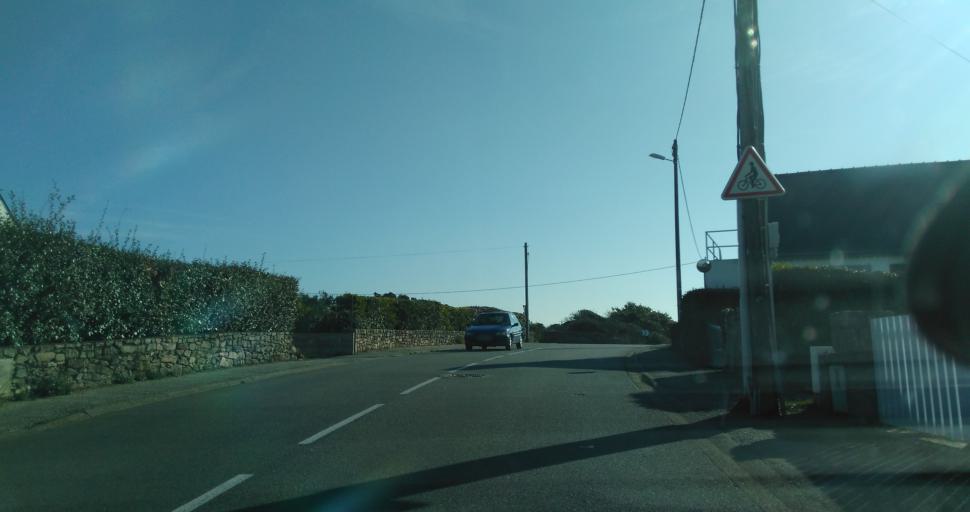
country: FR
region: Brittany
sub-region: Departement du Morbihan
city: Saint-Pierre-Quiberon
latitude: 47.5287
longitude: -3.1423
